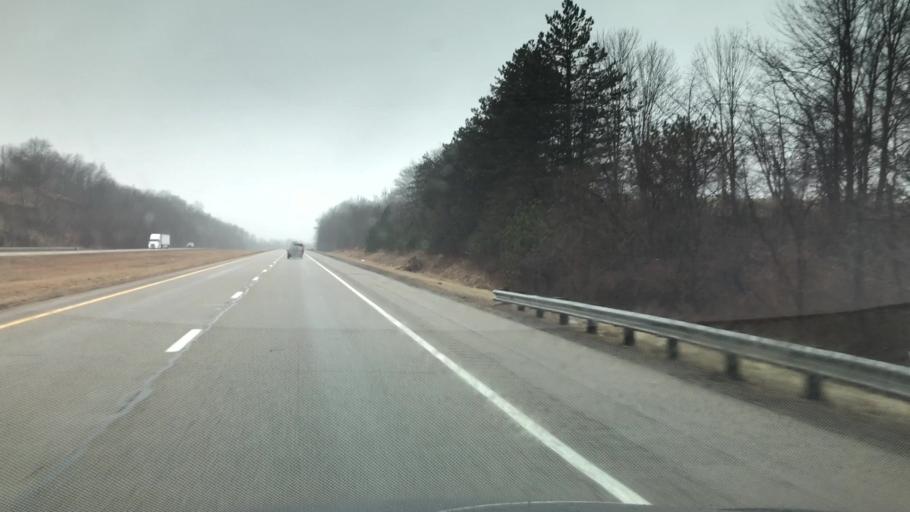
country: US
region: Ohio
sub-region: Muskingum County
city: Zanesville
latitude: 39.9455
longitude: -82.0775
